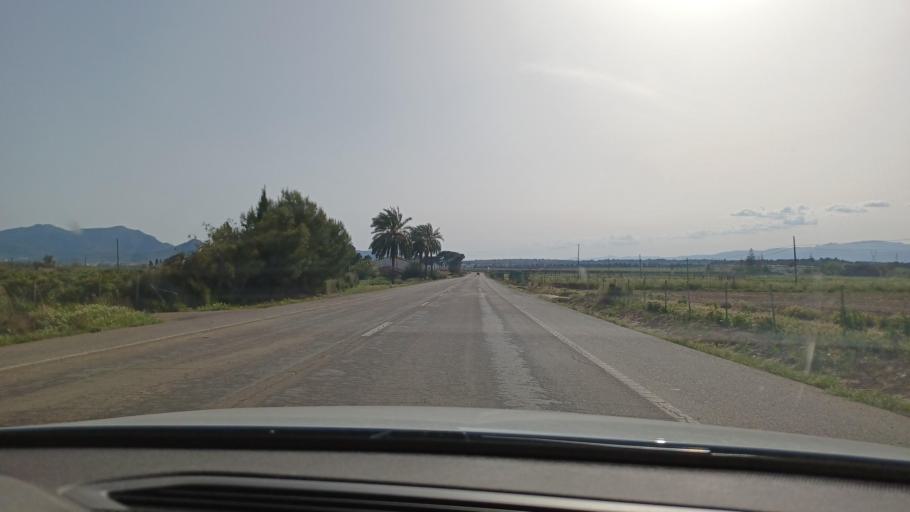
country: ES
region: Catalonia
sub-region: Provincia de Tarragona
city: Amposta
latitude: 40.7367
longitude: 0.6021
